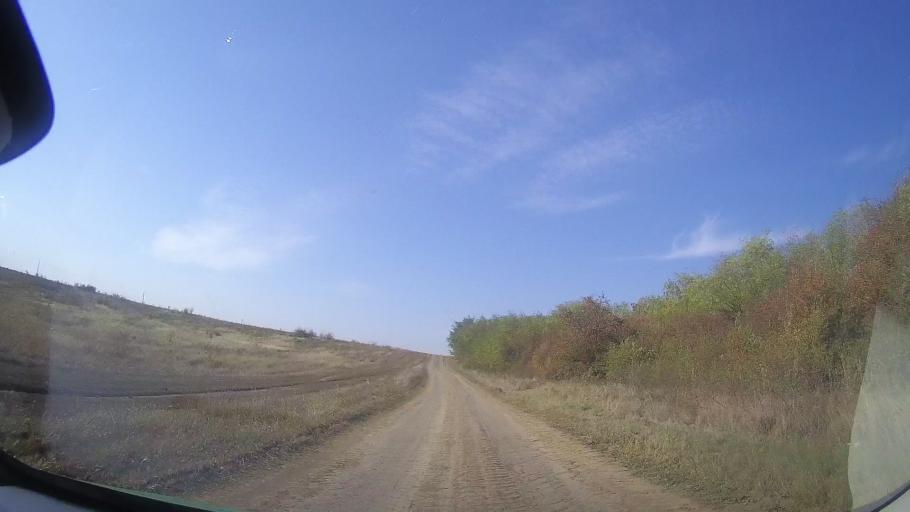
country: RO
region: Timis
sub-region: Oras Recas
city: Recas
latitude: 45.8796
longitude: 21.5319
